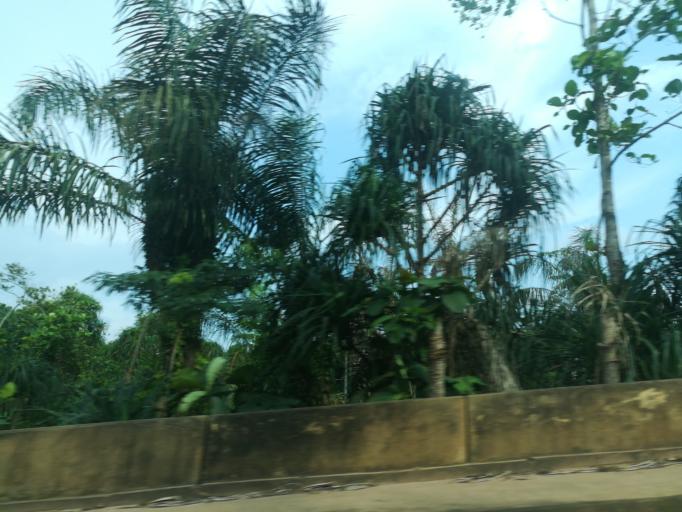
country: NG
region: Lagos
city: Ikorodu
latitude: 6.6262
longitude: 3.6642
